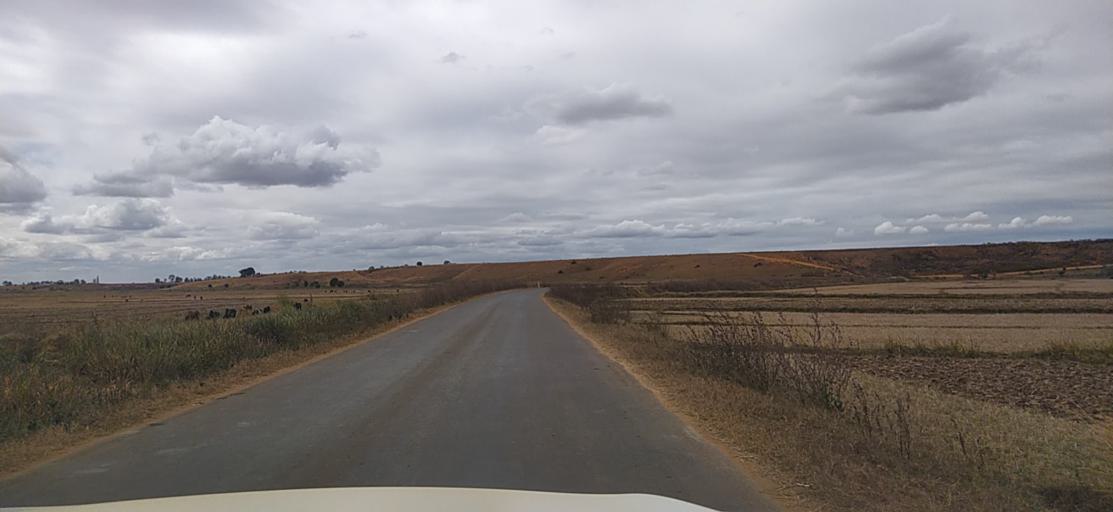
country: MG
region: Alaotra Mangoro
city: Ambatondrazaka
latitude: -17.9162
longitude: 48.2586
